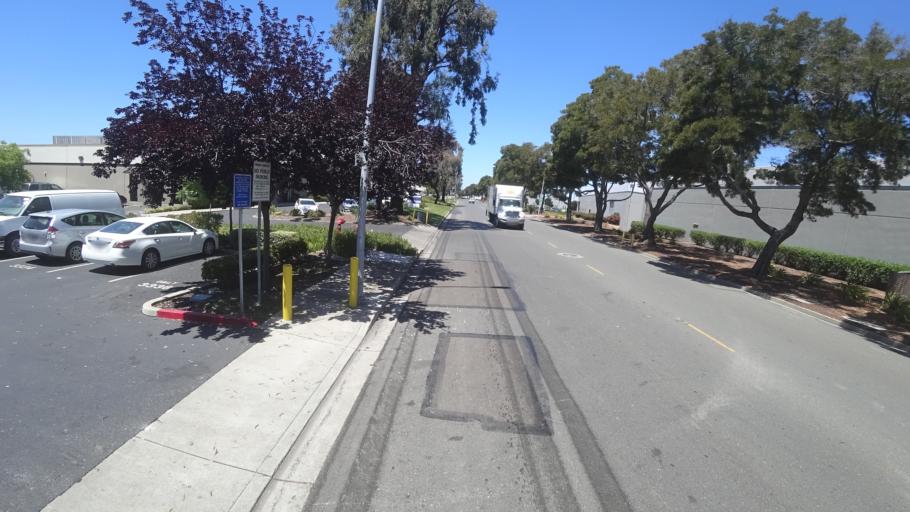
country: US
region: California
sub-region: Alameda County
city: Hayward
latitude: 37.6199
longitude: -122.1058
